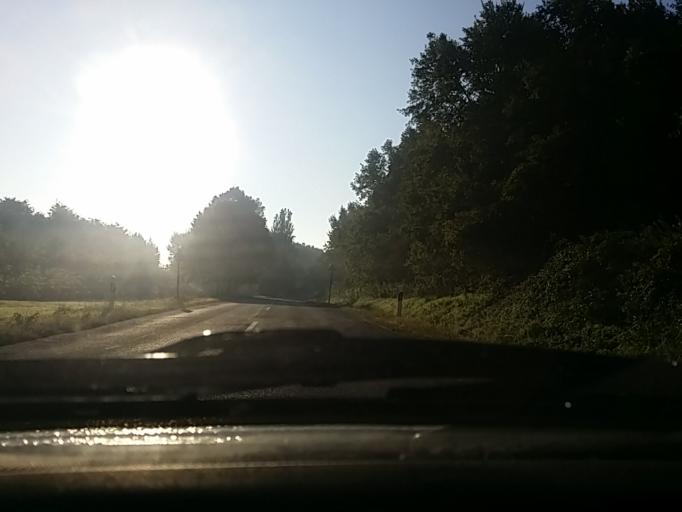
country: HU
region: Pest
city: Szob
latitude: 47.8013
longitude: 18.8545
